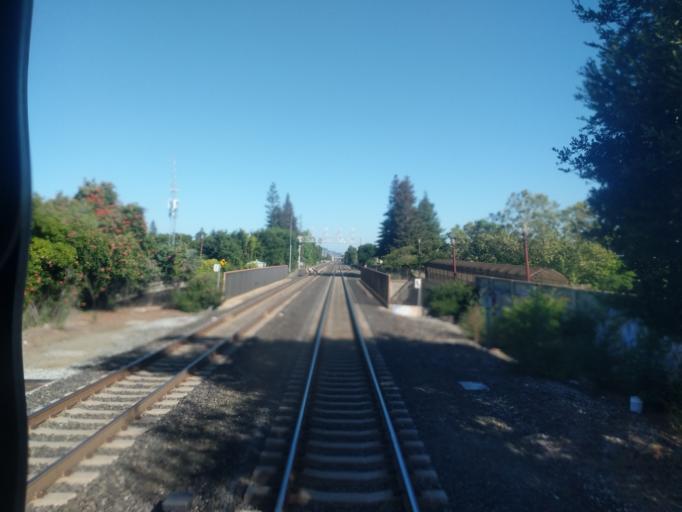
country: US
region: California
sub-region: San Mateo County
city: North Fair Oaks
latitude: 37.4696
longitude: -122.2055
